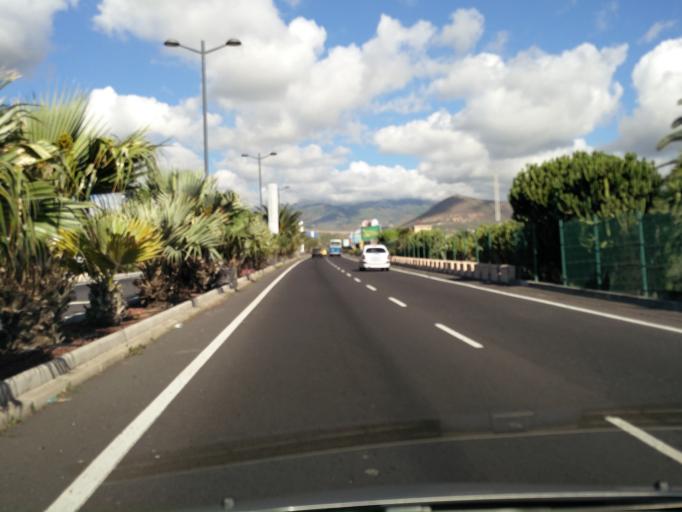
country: ES
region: Canary Islands
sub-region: Provincia de Santa Cruz de Tenerife
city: San Isidro
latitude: 28.0523
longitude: -16.5779
